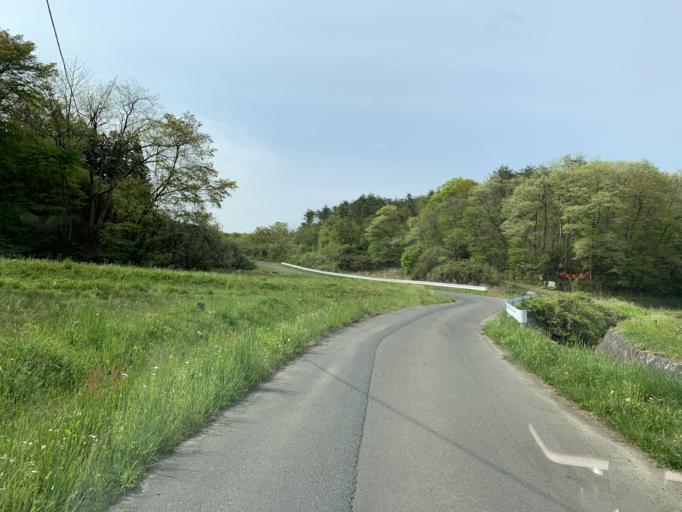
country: JP
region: Iwate
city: Ichinoseki
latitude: 38.9021
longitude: 141.0575
